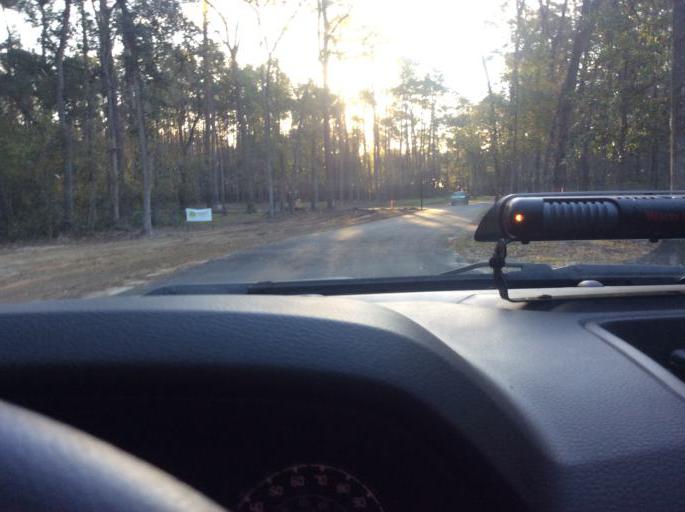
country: US
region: Georgia
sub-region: Chatham County
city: Georgetown
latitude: 31.9756
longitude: -81.2189
